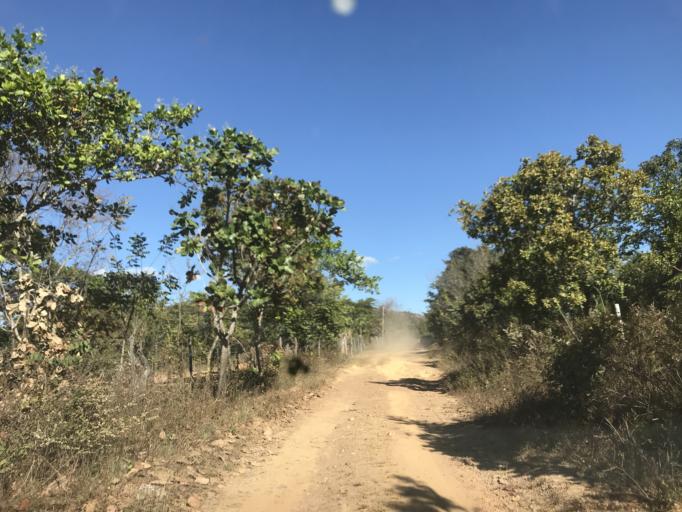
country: BR
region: Goias
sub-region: Padre Bernardo
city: Padre Bernardo
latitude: -15.4065
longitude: -48.2280
